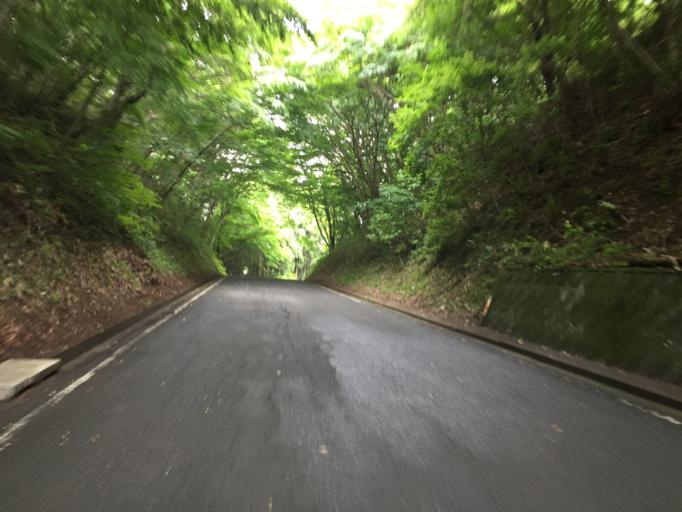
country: JP
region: Fukushima
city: Funehikimachi-funehiki
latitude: 37.4192
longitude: 140.7234
